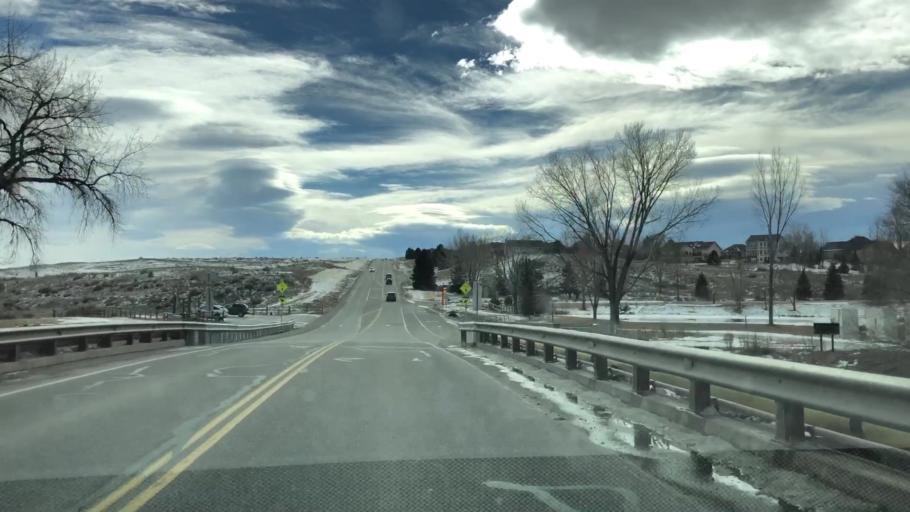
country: US
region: Colorado
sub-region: Weld County
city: Windsor
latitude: 40.4733
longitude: -104.9442
